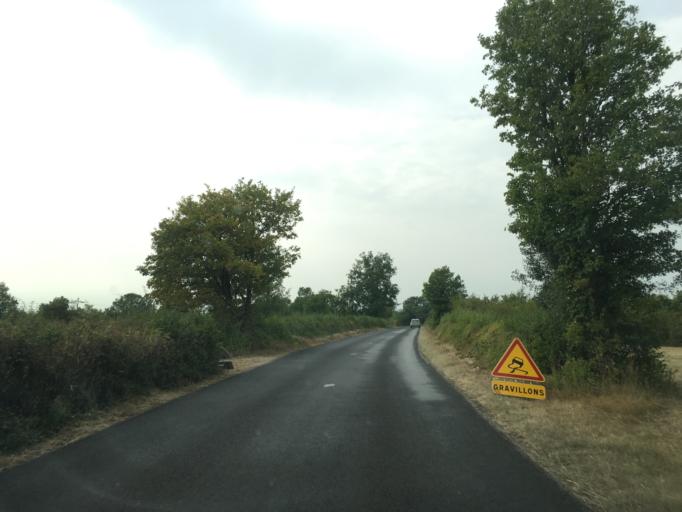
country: FR
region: Midi-Pyrenees
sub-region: Departement du Lot
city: Souillac
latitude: 44.8223
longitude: 1.5778
